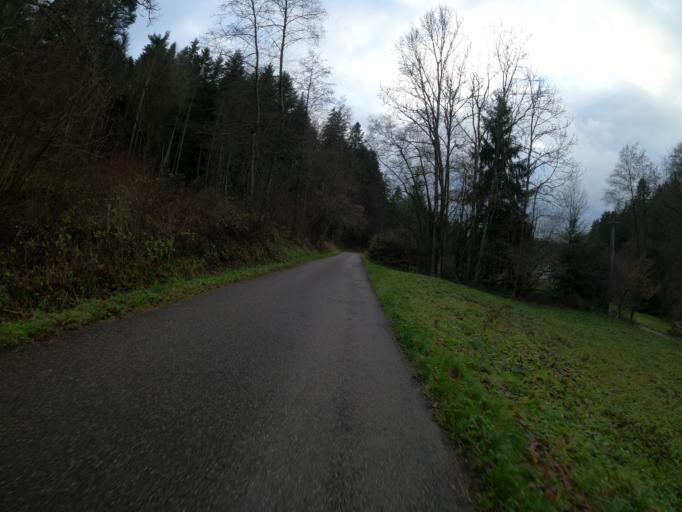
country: DE
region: Baden-Wuerttemberg
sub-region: Regierungsbezirk Stuttgart
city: Lorch
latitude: 48.7811
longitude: 9.7218
